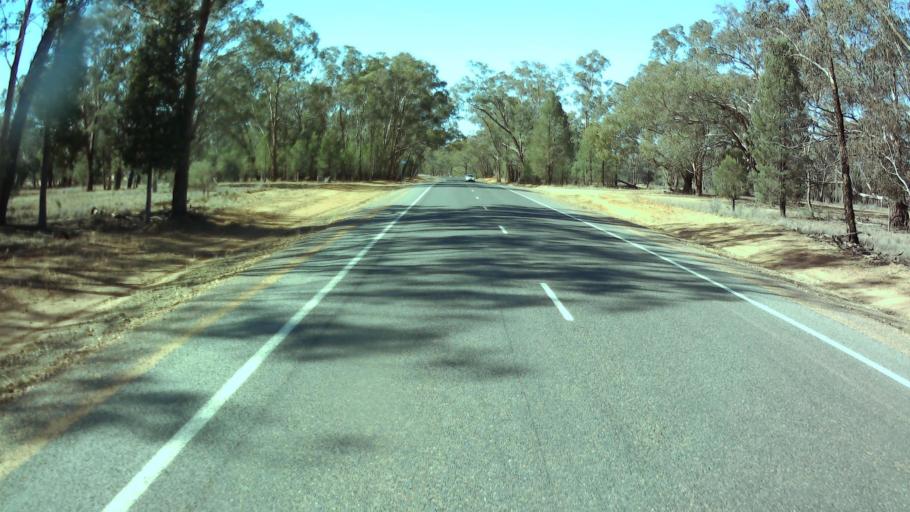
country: AU
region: New South Wales
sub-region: Weddin
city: Grenfell
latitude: -33.7609
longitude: 148.0822
